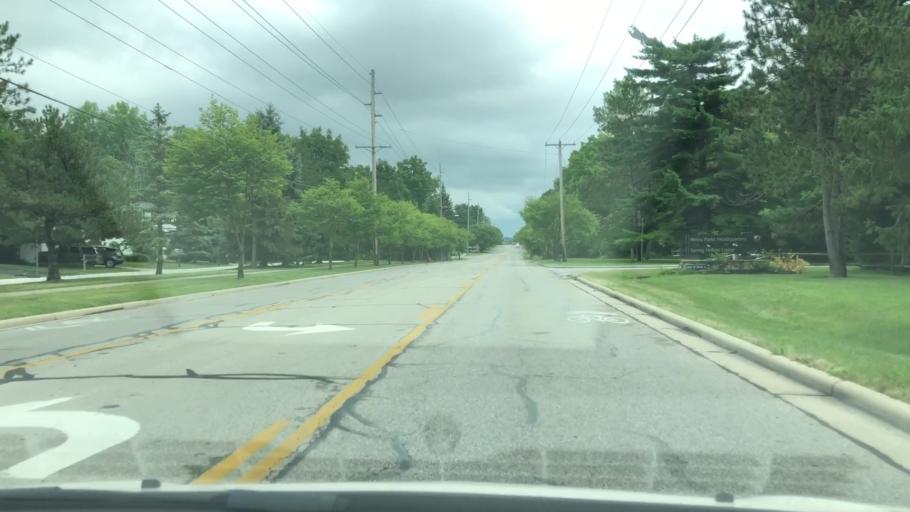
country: US
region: Ohio
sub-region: Franklin County
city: Westerville
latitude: 40.1255
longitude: -82.9678
